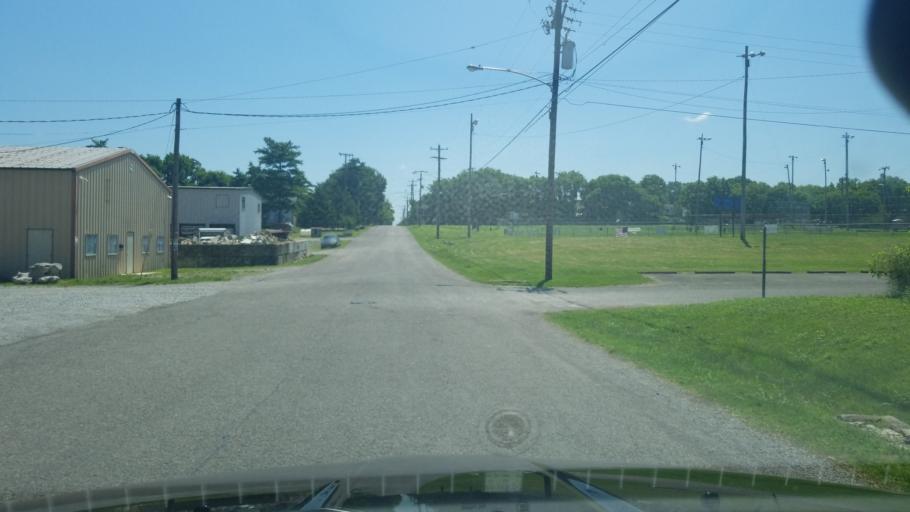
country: US
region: Tennessee
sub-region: Davidson County
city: Belle Meade
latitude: 36.1559
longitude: -86.8713
